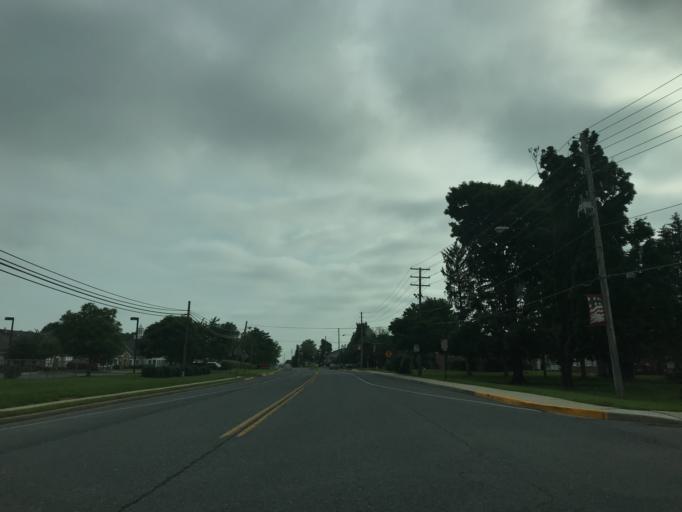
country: US
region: Maryland
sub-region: Frederick County
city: Walkersville
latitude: 39.4791
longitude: -77.3544
